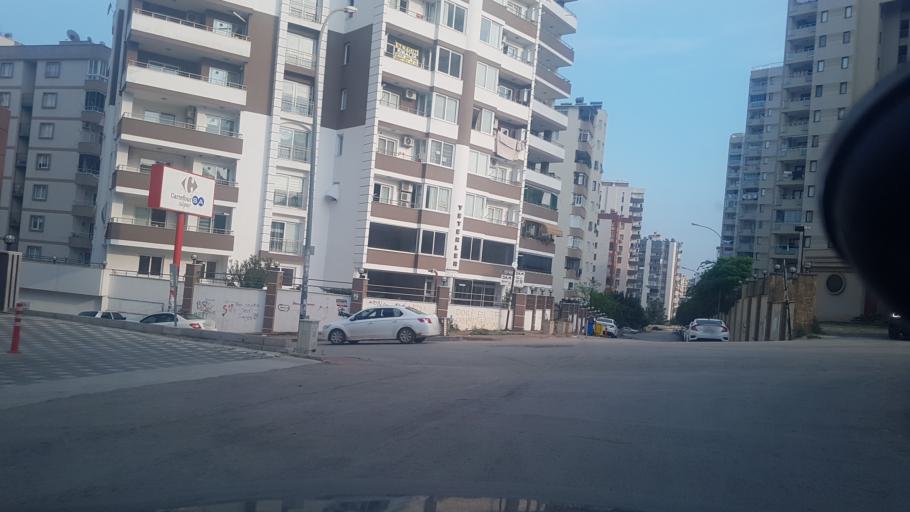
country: TR
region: Adana
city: Seyhan
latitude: 37.0449
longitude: 35.2764
